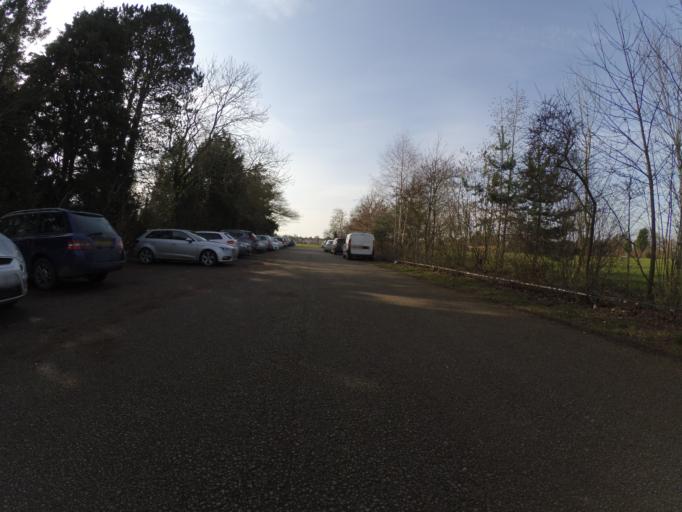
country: GB
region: England
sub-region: Warwickshire
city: Rugby
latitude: 52.3718
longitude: -1.2369
